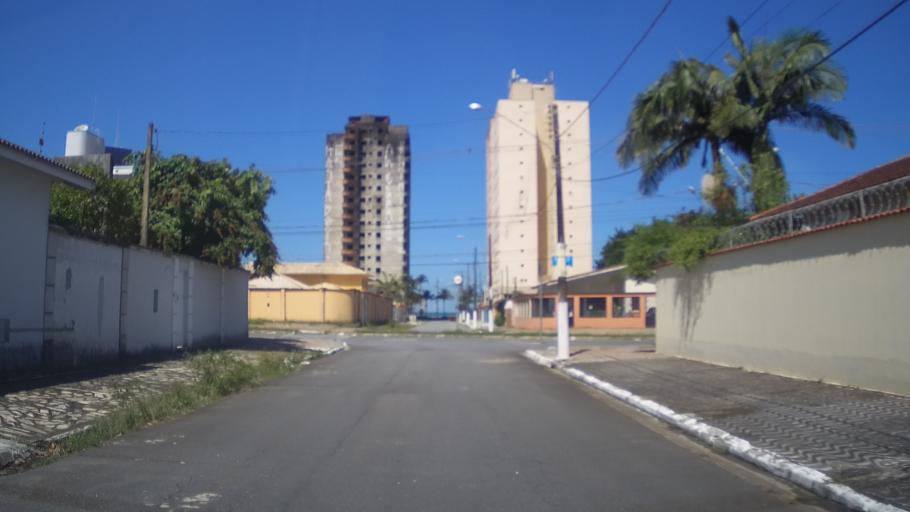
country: BR
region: Sao Paulo
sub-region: Mongagua
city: Mongagua
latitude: -24.0863
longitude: -46.6045
